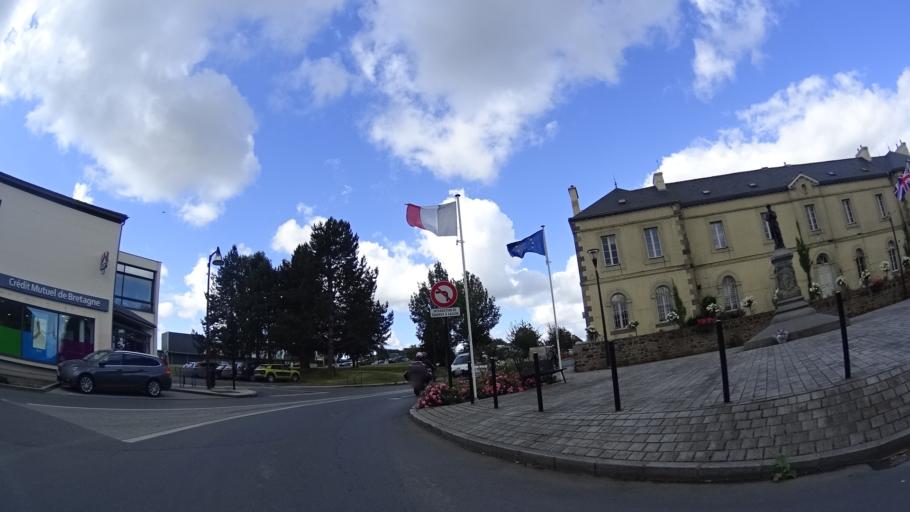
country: FR
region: Brittany
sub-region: Departement d'Ille-et-Vilaine
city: Tinteniac
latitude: 48.3291
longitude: -1.8376
